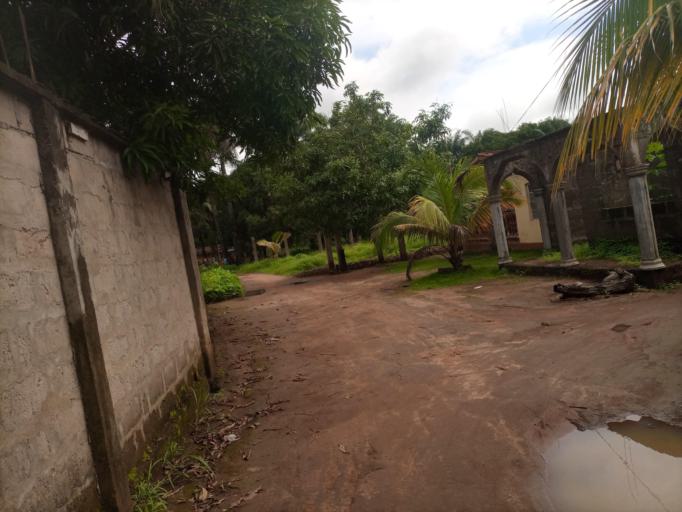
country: SL
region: Northern Province
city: Sawkta
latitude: 8.6252
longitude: -13.2022
